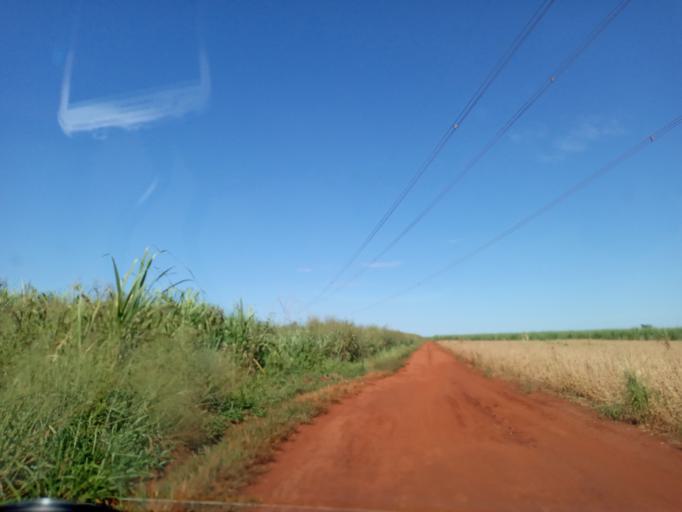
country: BR
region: Goias
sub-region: Itumbiara
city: Itumbiara
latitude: -18.4539
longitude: -49.1465
